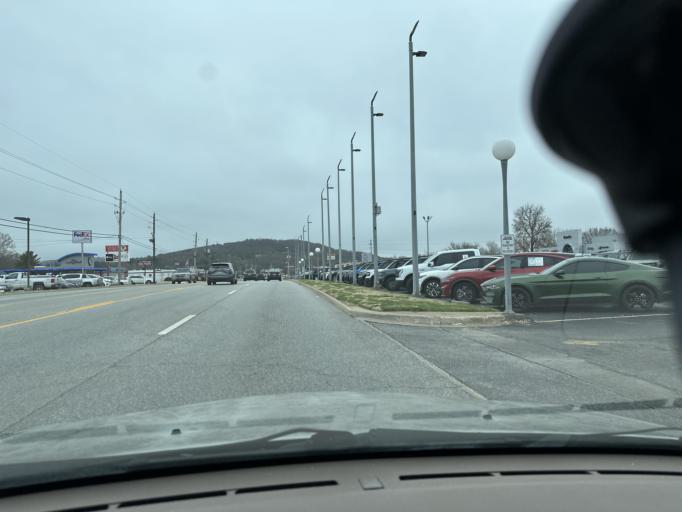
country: US
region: Arkansas
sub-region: Washington County
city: Johnson
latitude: 36.1126
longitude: -94.1452
